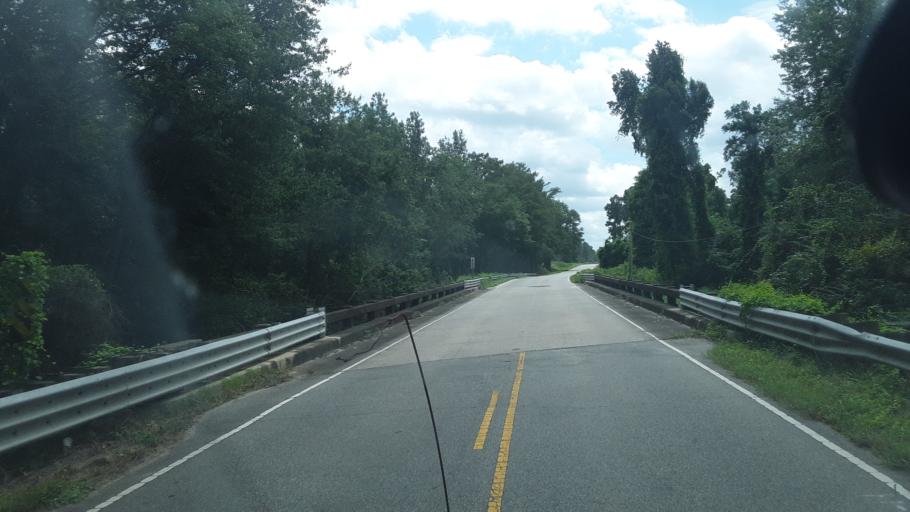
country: US
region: North Carolina
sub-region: Columbus County
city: Tabor City
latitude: 34.2762
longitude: -79.0418
